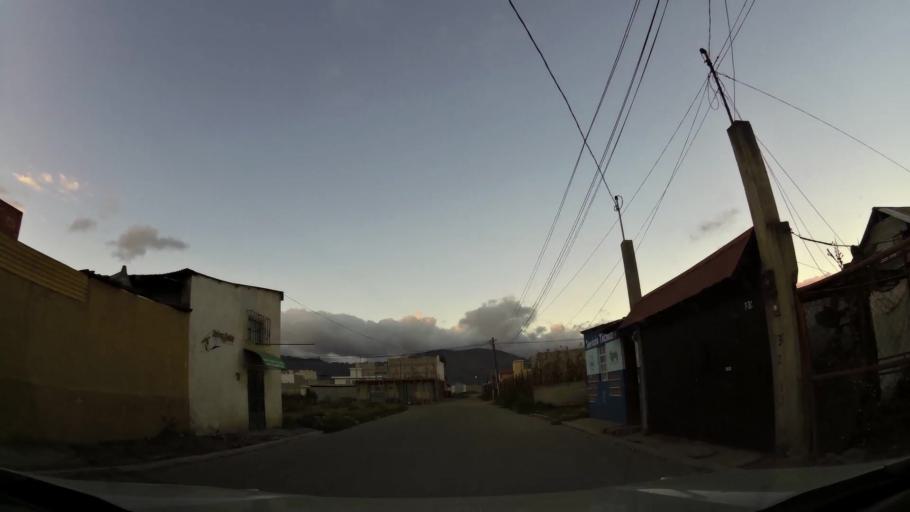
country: GT
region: Quetzaltenango
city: Quetzaltenango
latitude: 14.8534
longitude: -91.5105
